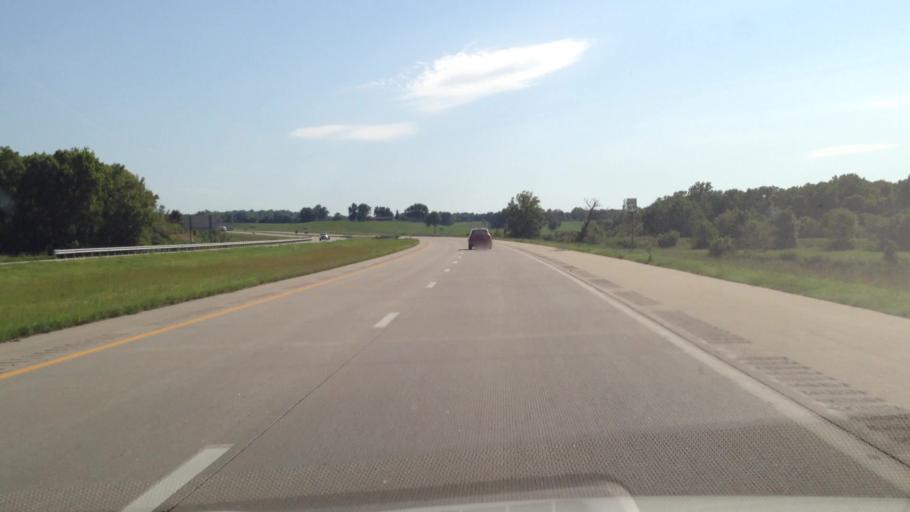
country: US
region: Kansas
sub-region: Linn County
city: Pleasanton
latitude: 38.1412
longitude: -94.7114
